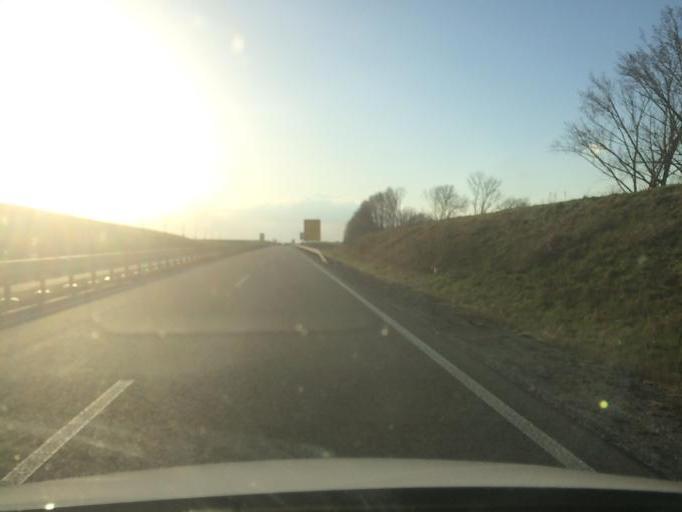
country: DE
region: Thuringia
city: Wipperdorf
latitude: 51.5017
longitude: 10.7048
